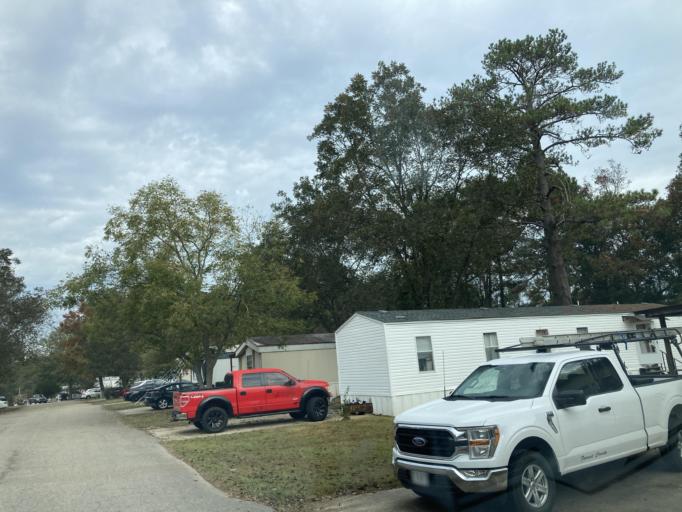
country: US
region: Mississippi
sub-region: Lamar County
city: West Hattiesburg
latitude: 31.3042
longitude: -89.3769
